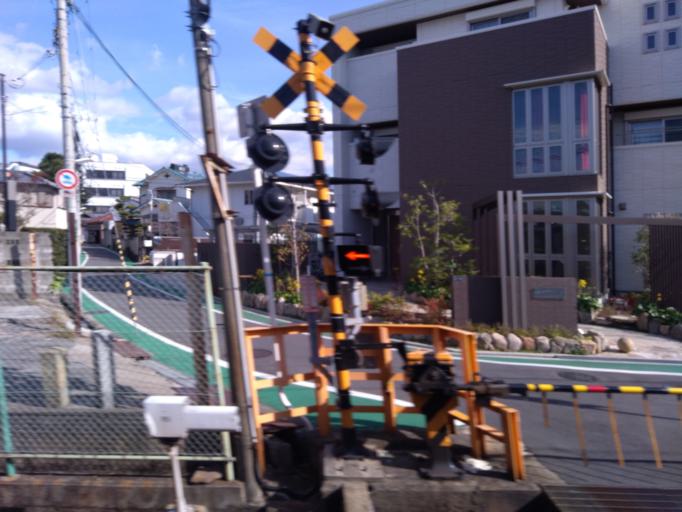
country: JP
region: Osaka
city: Ikeda
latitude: 34.8050
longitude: 135.4460
